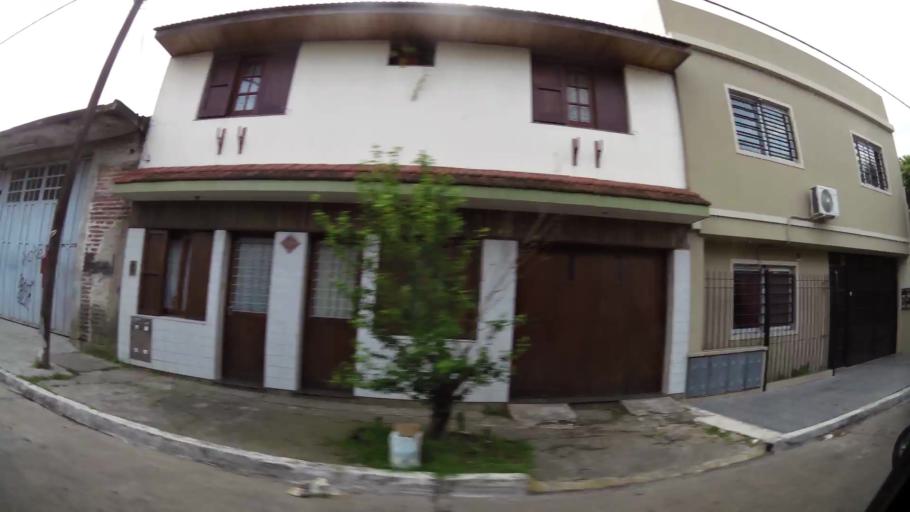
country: AR
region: Buenos Aires
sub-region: Partido de Quilmes
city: Quilmes
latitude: -34.7482
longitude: -58.2343
